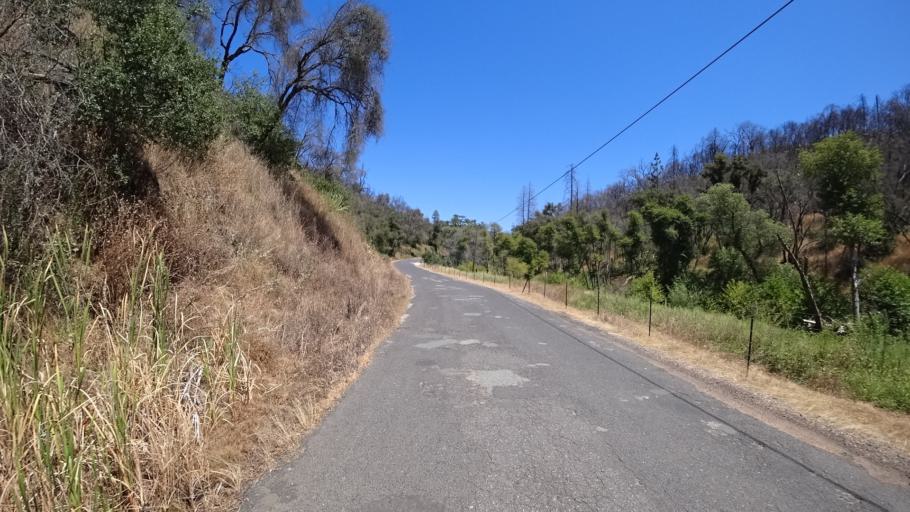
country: US
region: California
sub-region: Calaveras County
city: San Andreas
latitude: 38.2839
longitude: -120.6536
